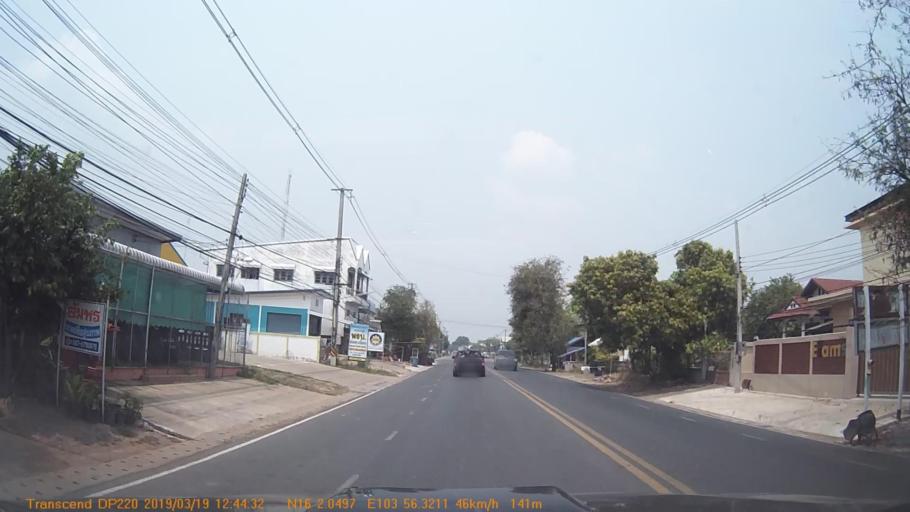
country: TH
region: Roi Et
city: Selaphum
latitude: 16.0342
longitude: 103.9387
